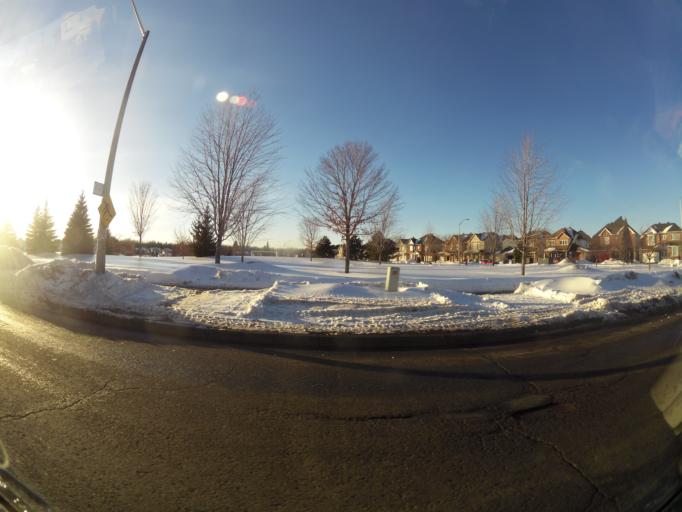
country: CA
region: Ontario
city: Ottawa
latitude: 45.4372
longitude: -75.5272
